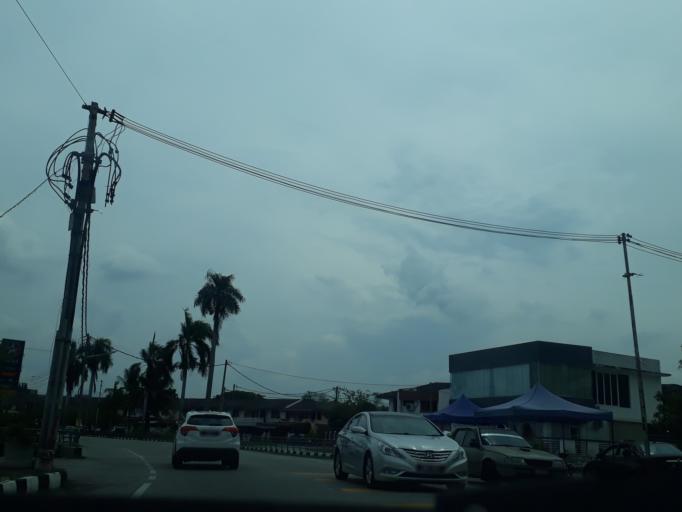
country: MY
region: Perak
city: Ipoh
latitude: 4.5954
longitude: 101.1283
